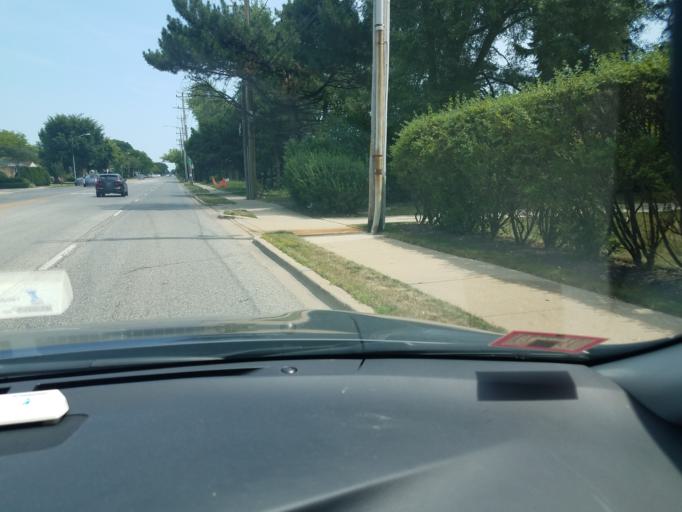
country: US
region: Illinois
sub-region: Cook County
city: Skokie
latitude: 42.0407
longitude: -87.7456
